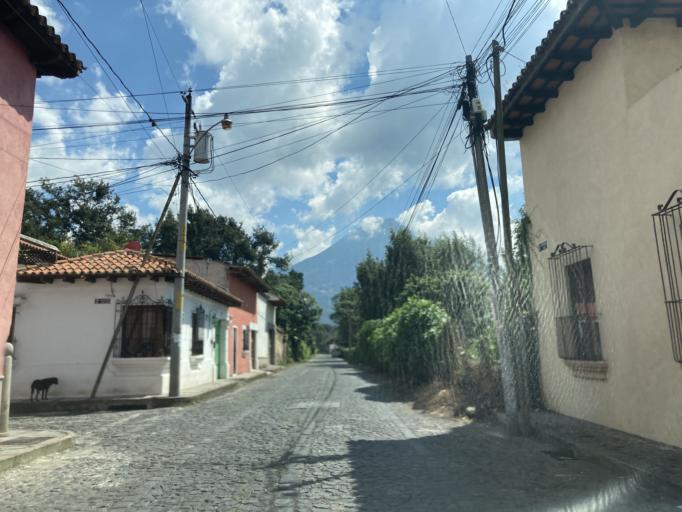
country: GT
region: Sacatepequez
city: Antigua Guatemala
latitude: 14.5507
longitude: -90.7332
